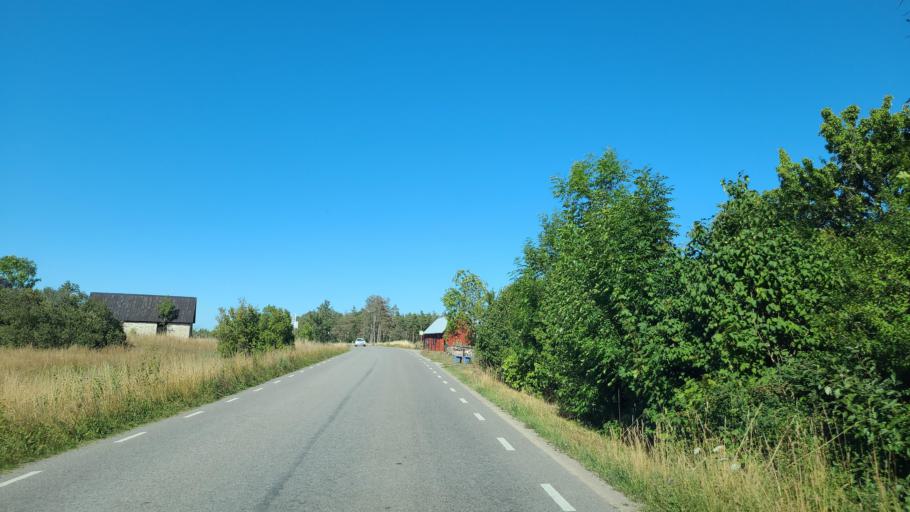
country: SE
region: Kalmar
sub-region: Borgholms Kommun
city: Borgholm
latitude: 56.9302
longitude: 16.8508
